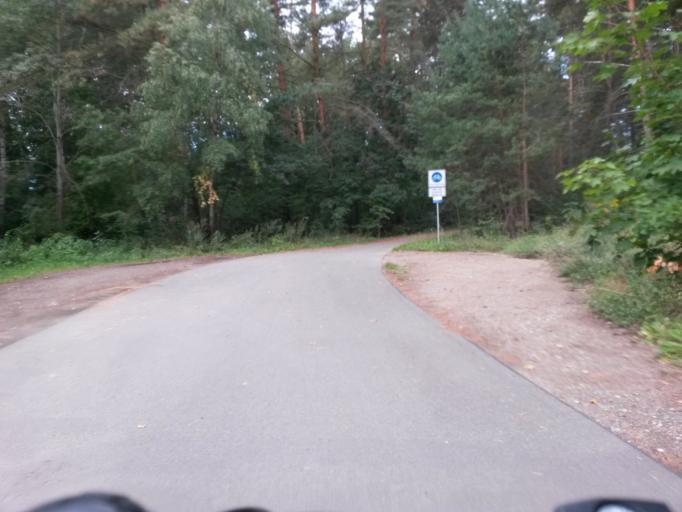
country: DE
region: Brandenburg
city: Templin
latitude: 53.1376
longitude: 13.5481
